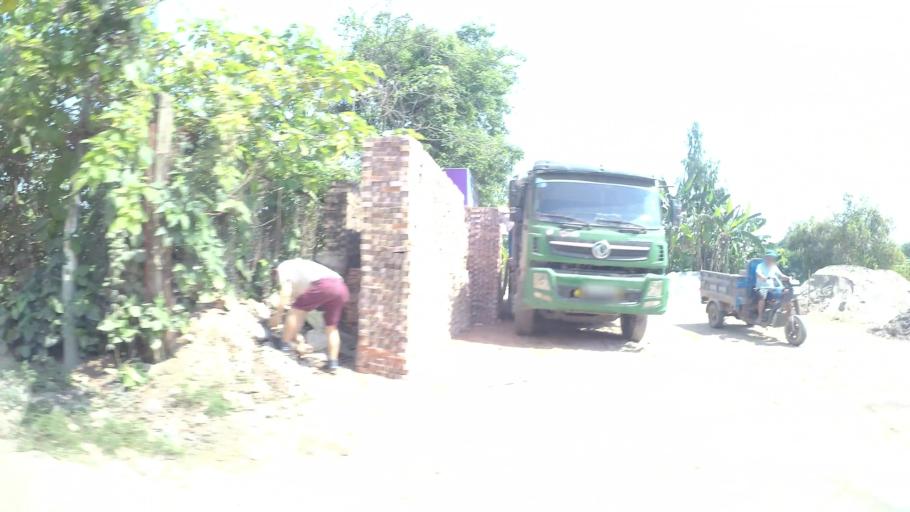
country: VN
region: Ha Noi
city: Hoan Kiem
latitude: 21.0566
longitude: 105.8782
